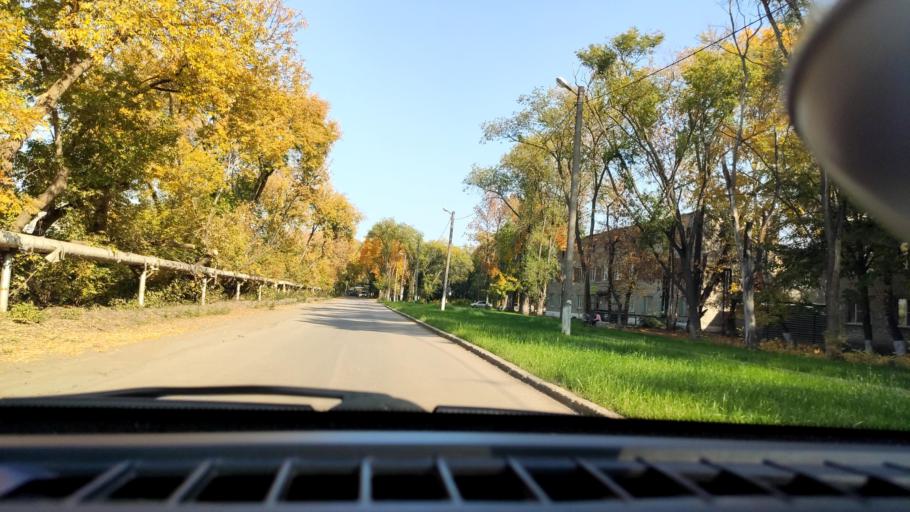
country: RU
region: Samara
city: Smyshlyayevka
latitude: 53.1893
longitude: 50.2887
